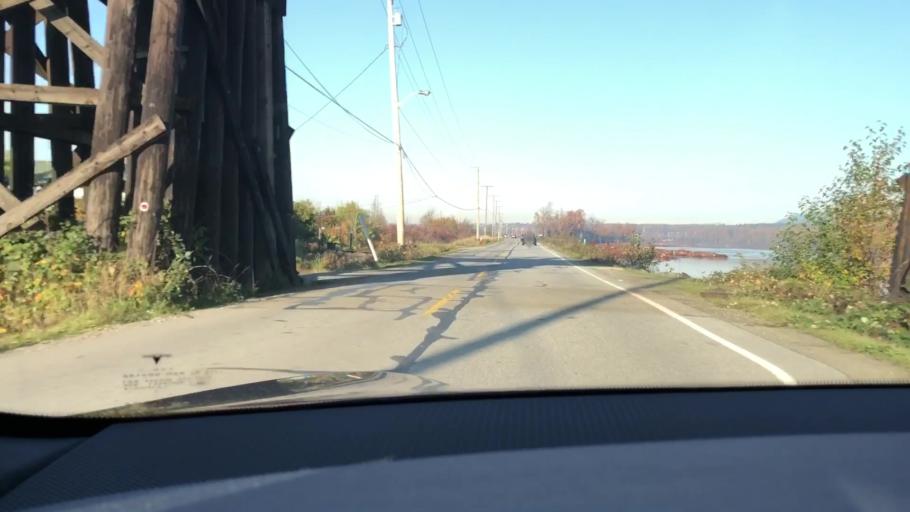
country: CA
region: British Columbia
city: New Westminster
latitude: 49.1823
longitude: -122.9887
